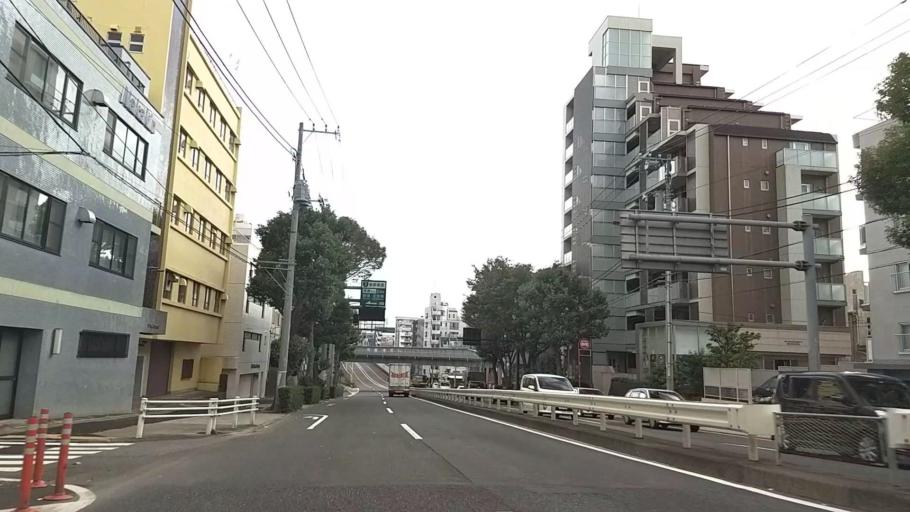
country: JP
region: Tokyo
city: Tokyo
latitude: 35.6061
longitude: 139.6959
